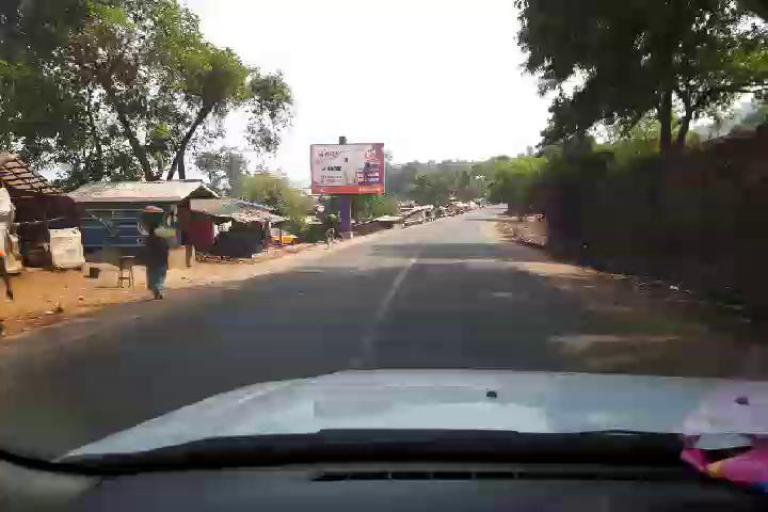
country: SL
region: Western Area
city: Waterloo
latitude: 8.2108
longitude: -13.1025
